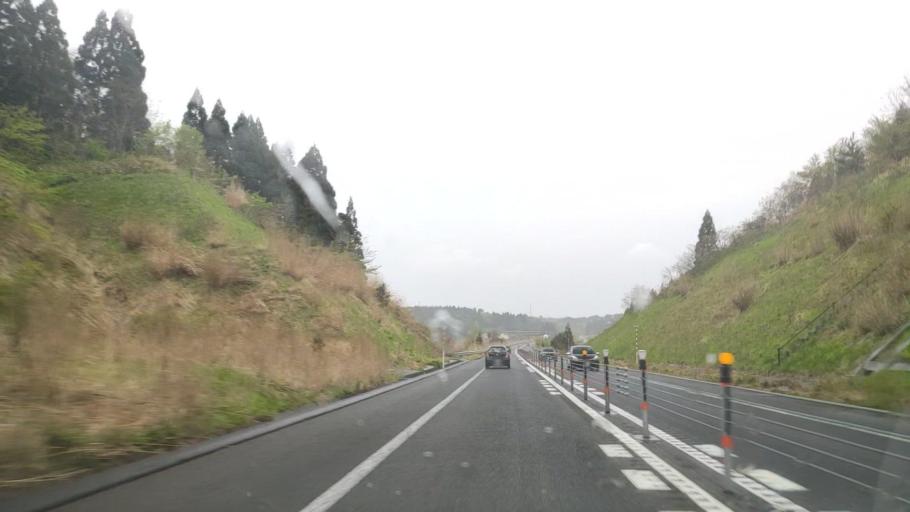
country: JP
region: Akita
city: Noshiromachi
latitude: 40.1893
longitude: 140.1031
